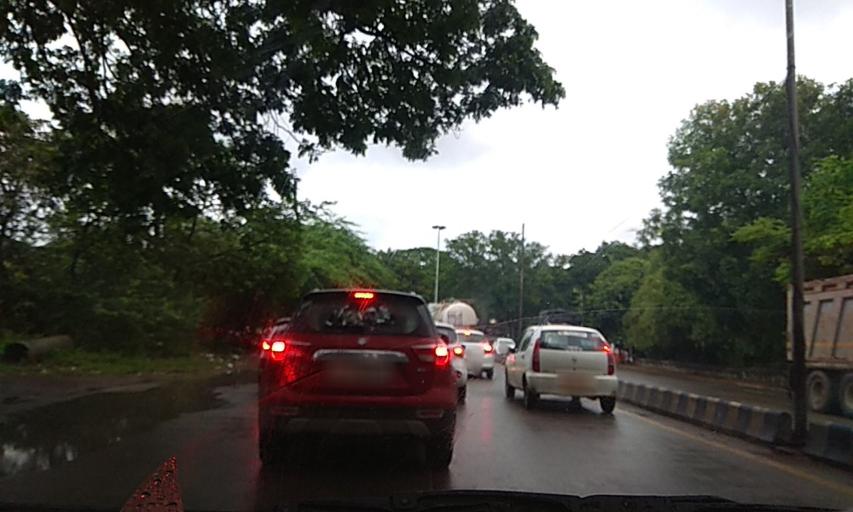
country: IN
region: Maharashtra
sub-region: Pune Division
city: Khadki
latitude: 18.5498
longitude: 73.8542
